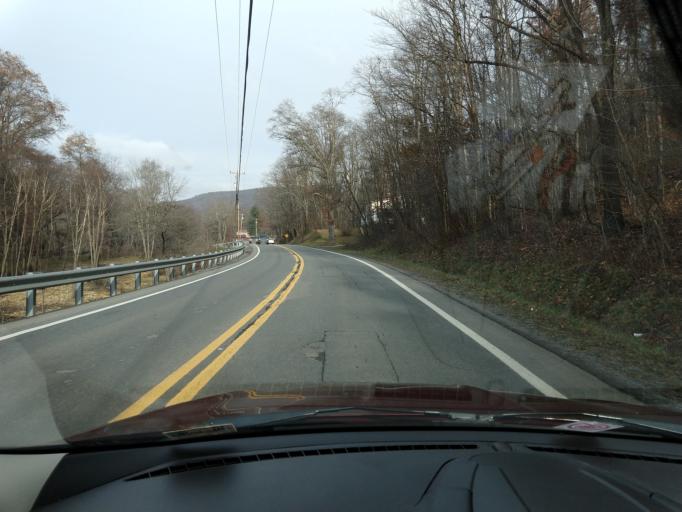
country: US
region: West Virginia
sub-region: Greenbrier County
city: Rainelle
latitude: 37.9726
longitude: -80.7081
